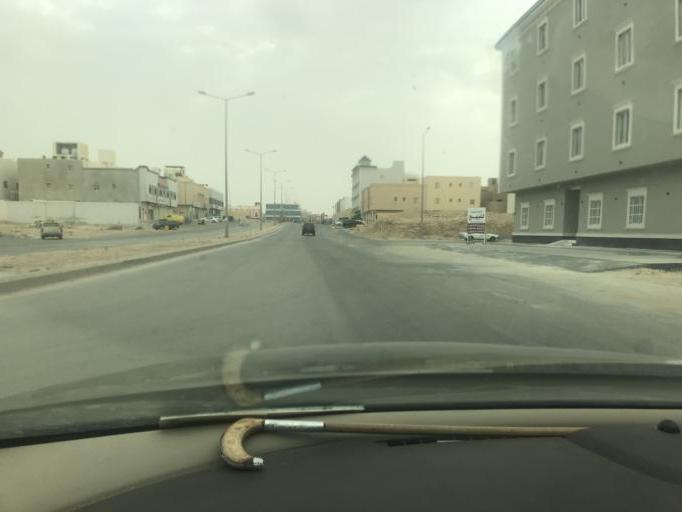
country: SA
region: Ar Riyad
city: Riyadh
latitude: 24.8116
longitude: 46.6042
